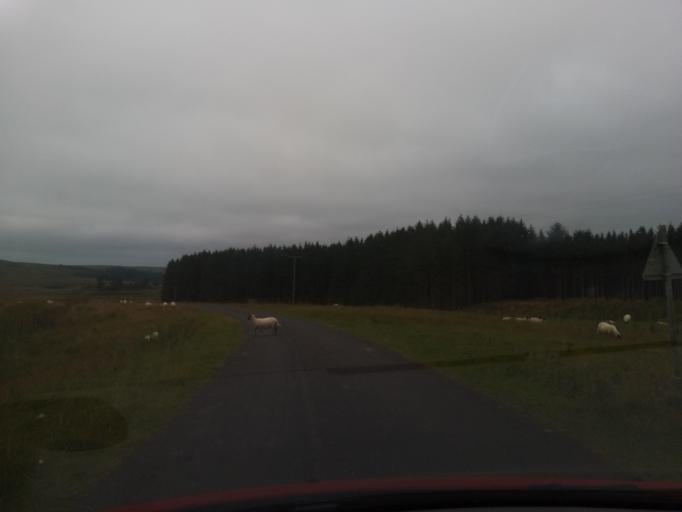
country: GB
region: England
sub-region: Northumberland
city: Rochester
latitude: 55.2902
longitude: -2.2163
